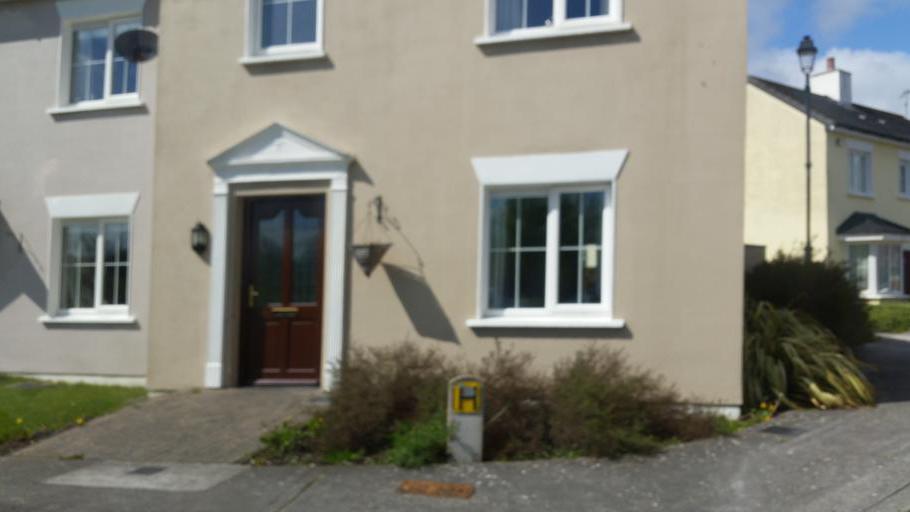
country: IE
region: Leinster
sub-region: Laois
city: Portlaoise
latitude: 53.0402
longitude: -7.2978
